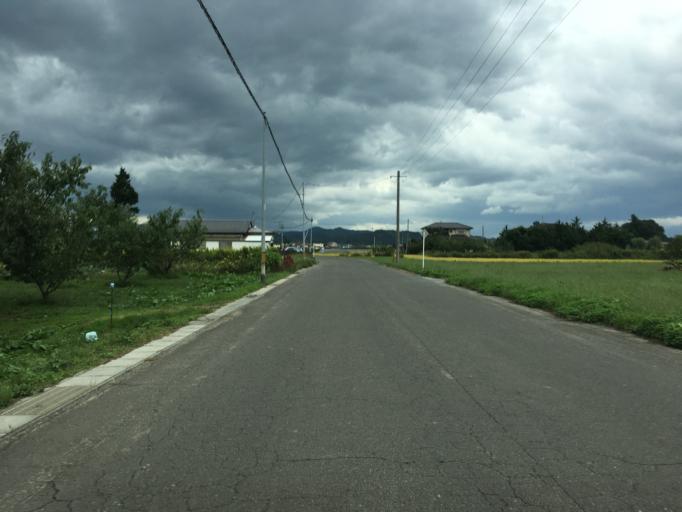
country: JP
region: Fukushima
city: Hobaramachi
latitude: 37.8339
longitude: 140.5486
